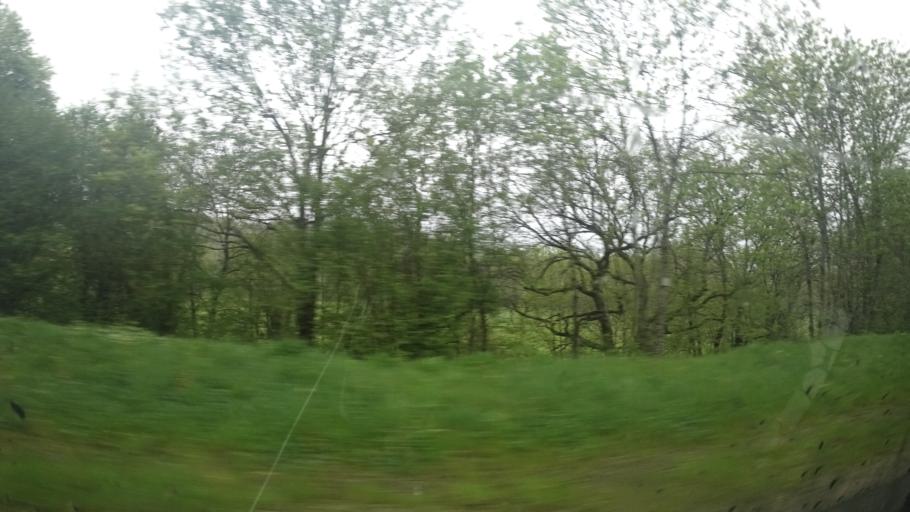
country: FR
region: Midi-Pyrenees
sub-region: Departement de l'Aveyron
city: Laissac
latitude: 44.3083
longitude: 2.8132
